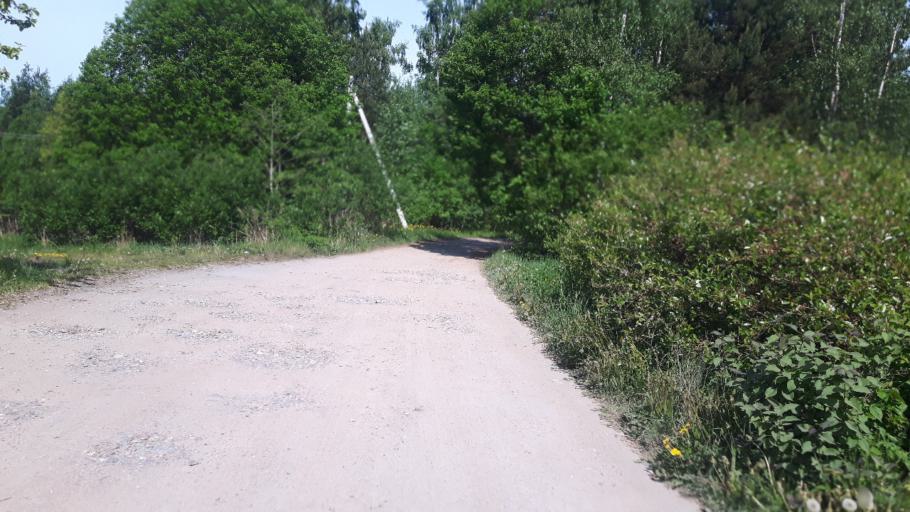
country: RU
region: Leningrad
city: Vistino
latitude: 59.6732
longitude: 28.4452
